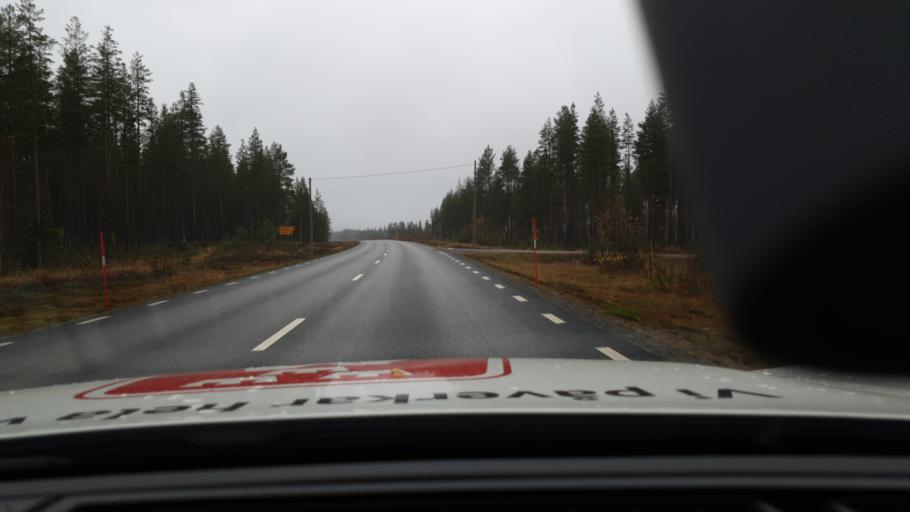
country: SE
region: Norrbotten
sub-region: Overkalix Kommun
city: OEverkalix
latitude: 66.6200
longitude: 22.2308
